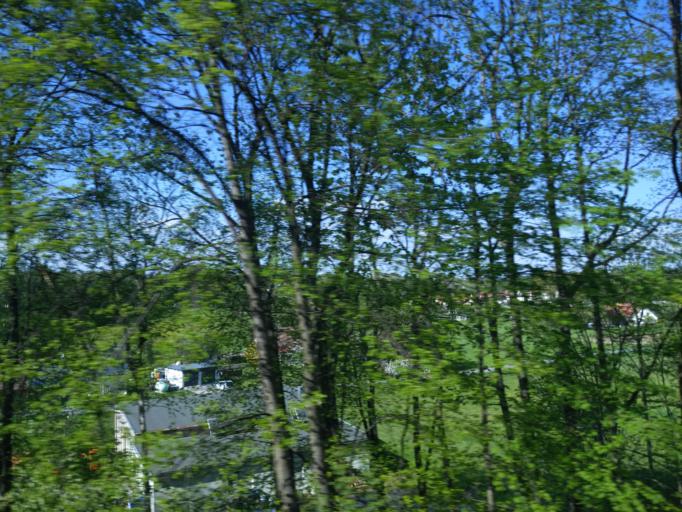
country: DE
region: Saxony
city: Demitz-Thumitz
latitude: 51.1393
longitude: 14.2492
